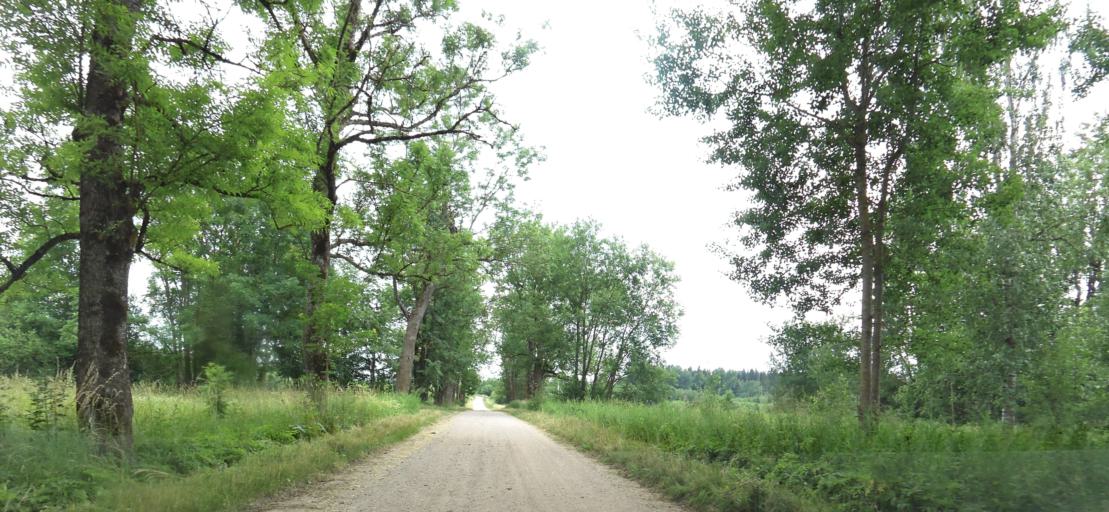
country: LT
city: Obeliai
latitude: 56.1819
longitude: 25.0439
